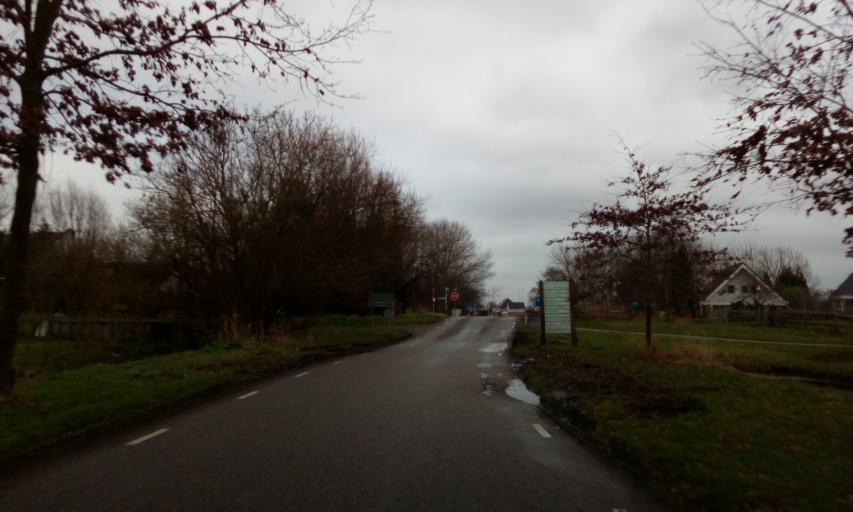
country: NL
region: South Holland
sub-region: Gemeente Lansingerland
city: Bleiswijk
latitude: 51.9741
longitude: 4.5558
